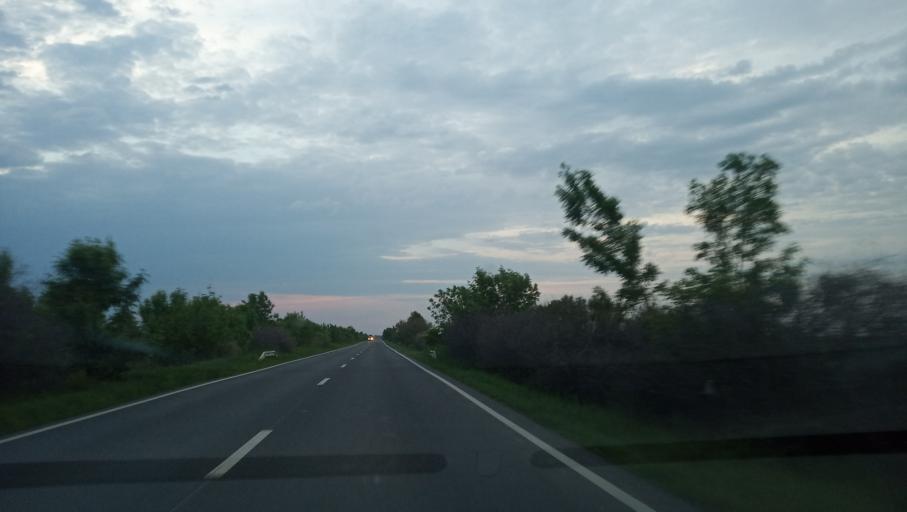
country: RO
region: Timis
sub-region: Comuna Jebel
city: Jebel
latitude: 45.5344
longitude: 21.2285
